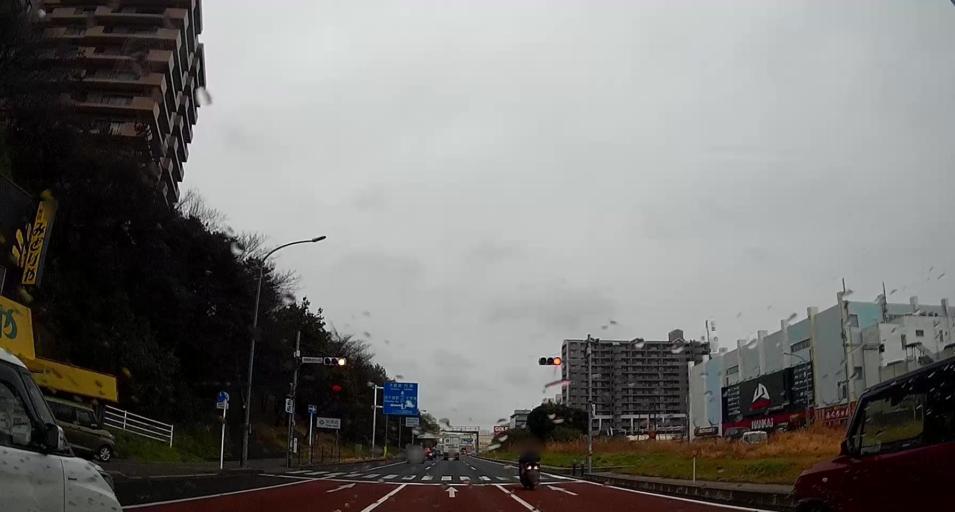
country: JP
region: Chiba
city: Chiba
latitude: 35.6202
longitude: 140.0965
